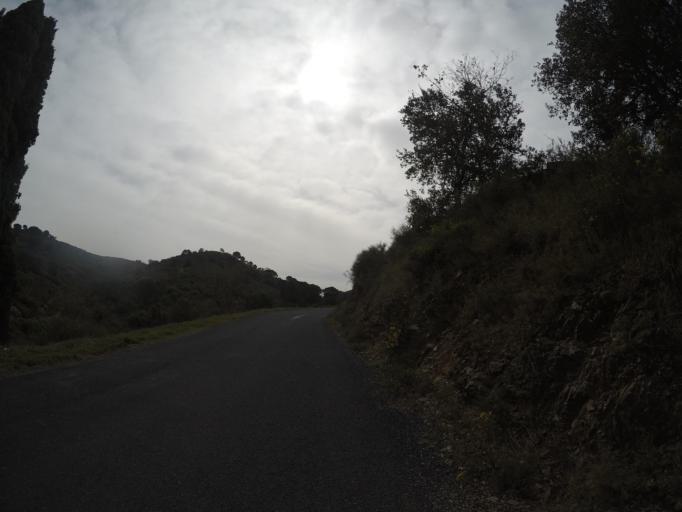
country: FR
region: Languedoc-Roussillon
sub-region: Departement des Pyrenees-Orientales
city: Estagel
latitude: 42.7455
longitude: 2.7249
